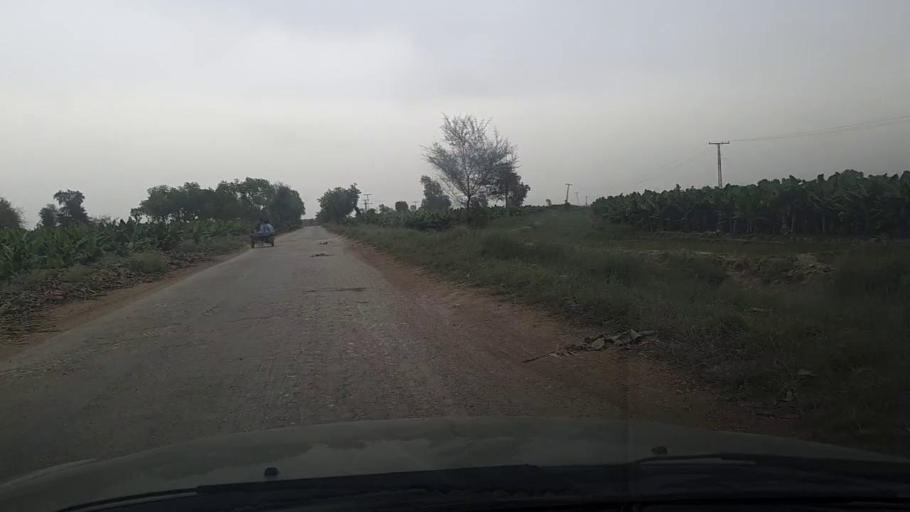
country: PK
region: Sindh
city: Daur
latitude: 26.3871
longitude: 68.1881
